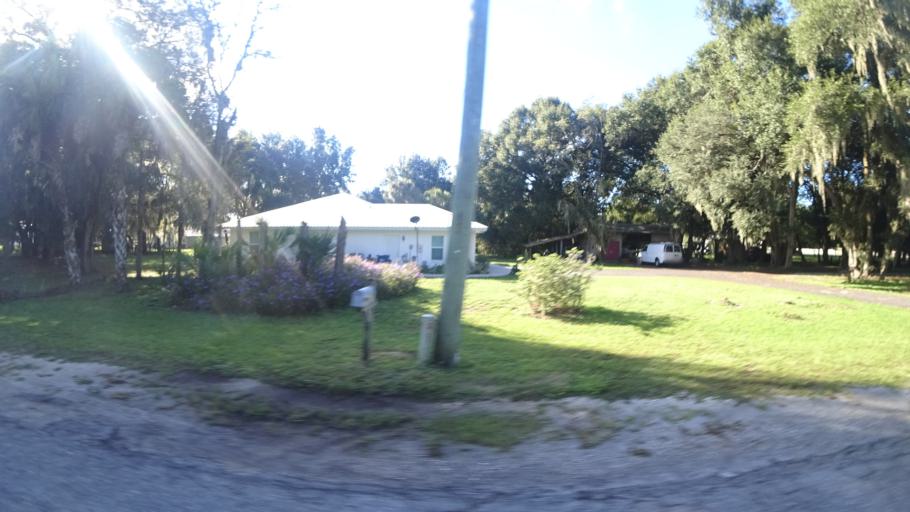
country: US
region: Florida
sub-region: Manatee County
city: Memphis
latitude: 27.5941
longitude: -82.5262
